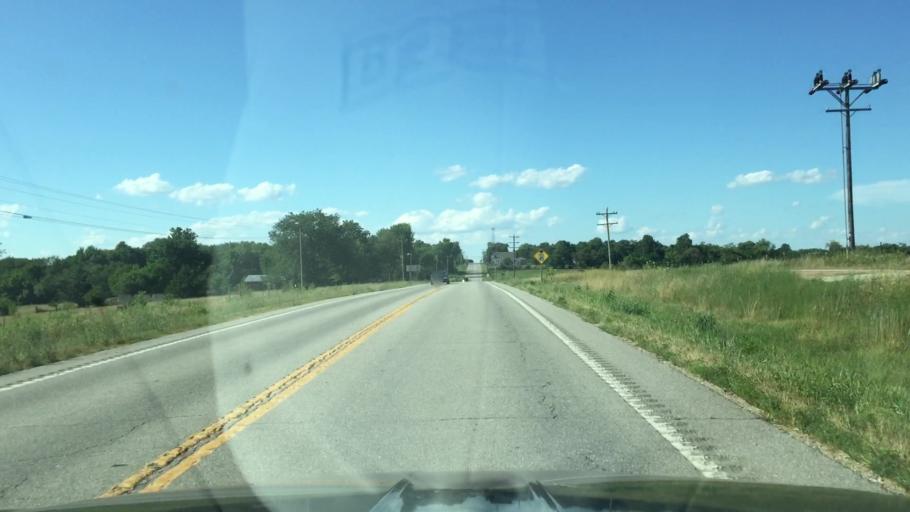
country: US
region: Missouri
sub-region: Moniteau County
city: Tipton
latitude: 38.5604
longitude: -92.7973
